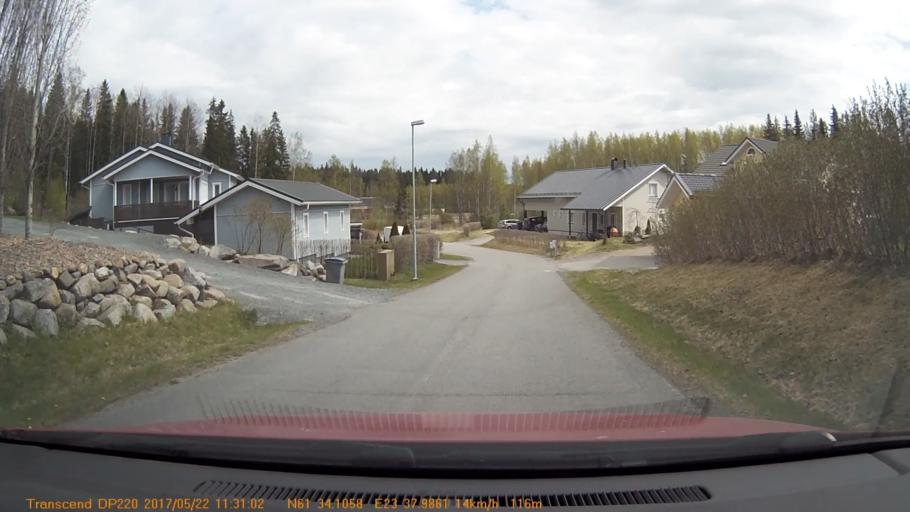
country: FI
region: Pirkanmaa
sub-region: Tampere
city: Yloejaervi
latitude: 61.5684
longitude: 23.6330
